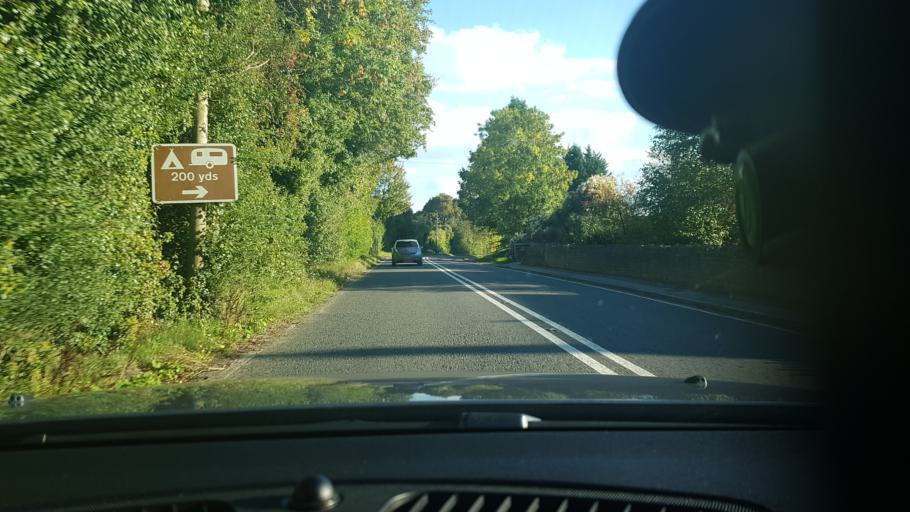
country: GB
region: England
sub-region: Gloucestershire
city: Cirencester
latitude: 51.7493
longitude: -1.9715
